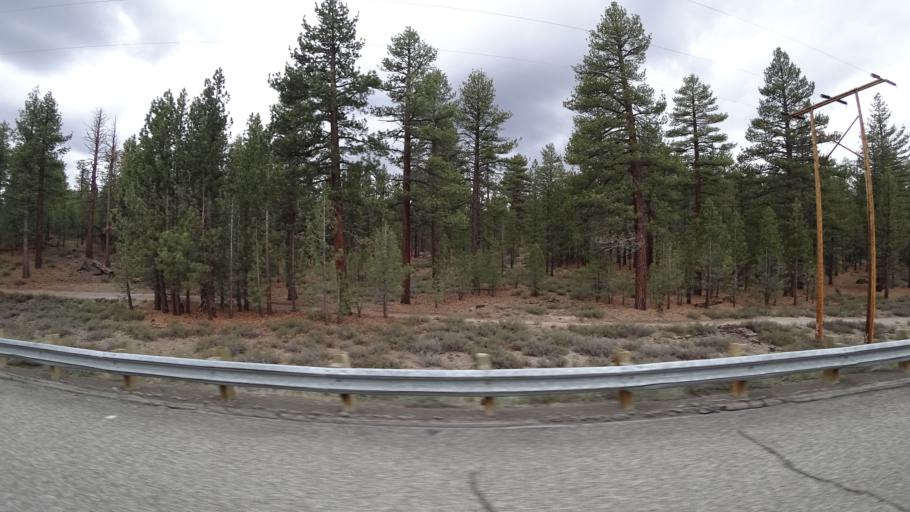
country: US
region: California
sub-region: Mono County
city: Mammoth Lakes
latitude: 37.7201
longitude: -118.9599
